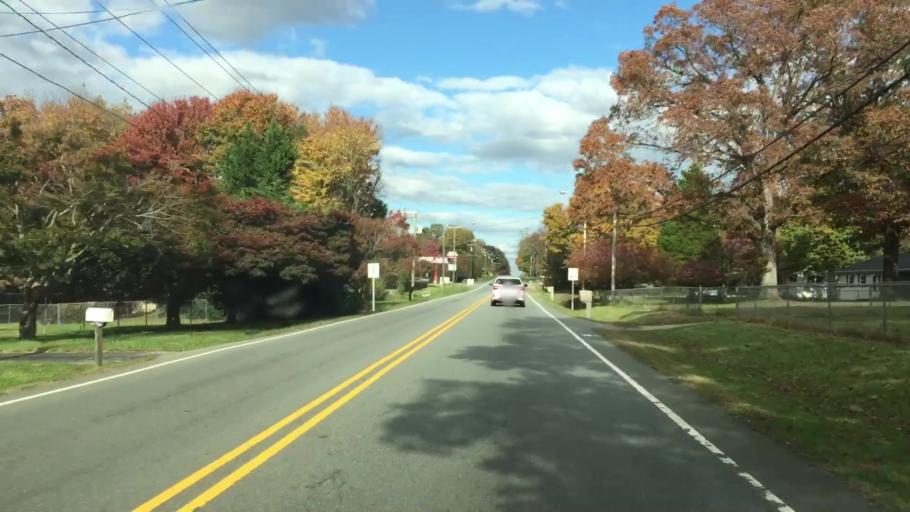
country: US
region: North Carolina
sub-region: Forsyth County
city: Walkertown
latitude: 36.1245
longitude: -80.1780
